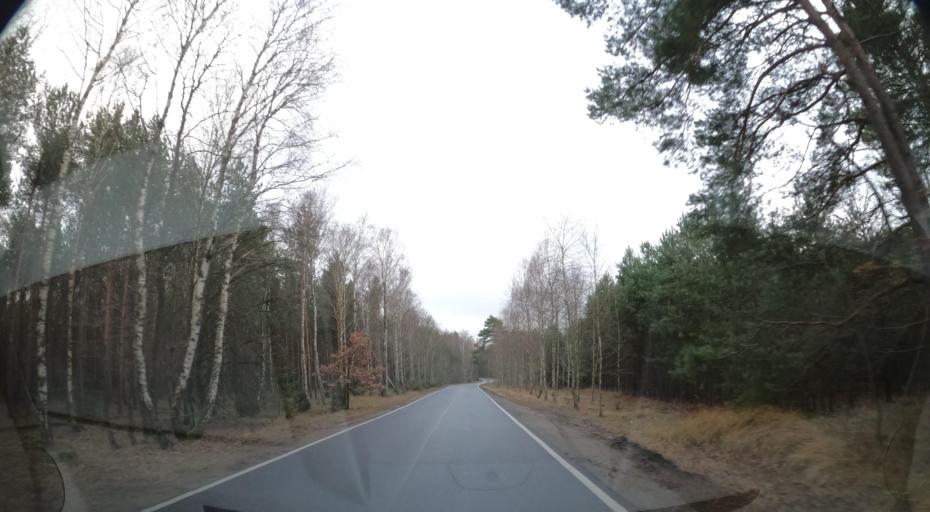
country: PL
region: Kujawsko-Pomorskie
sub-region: Powiat bydgoski
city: Solec Kujawski
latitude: 53.0586
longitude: 18.2285
